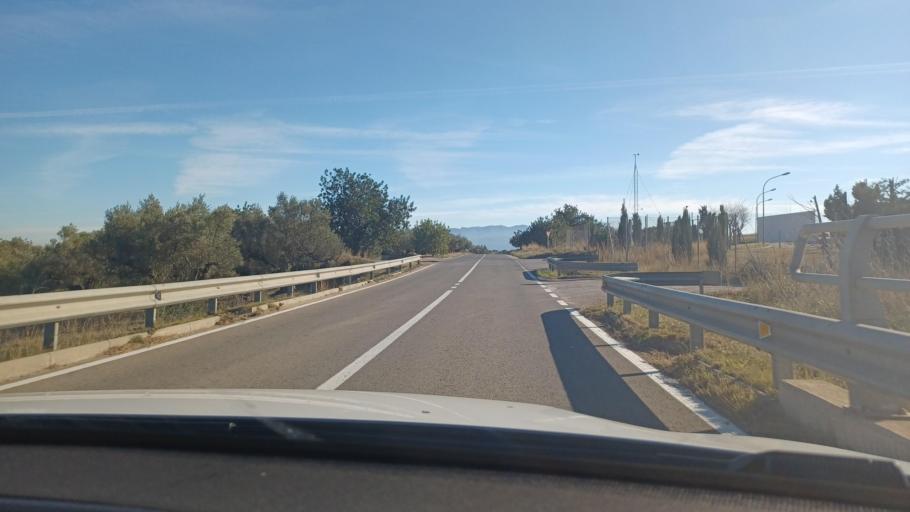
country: ES
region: Catalonia
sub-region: Provincia de Tarragona
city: Mas de Barberans
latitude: 40.7189
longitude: 0.3994
